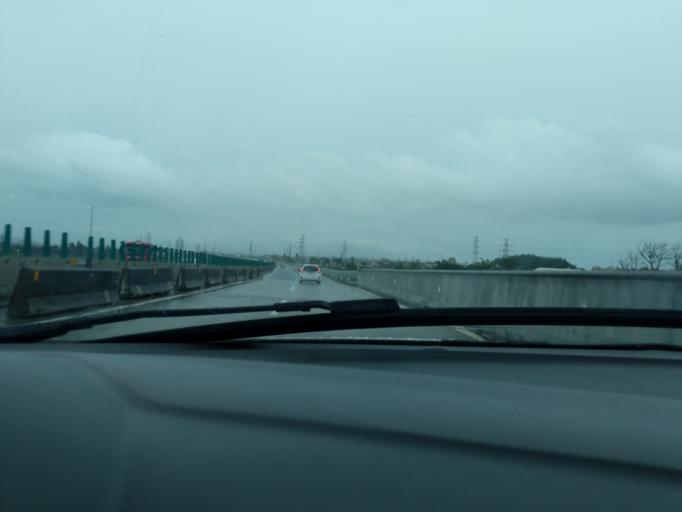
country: CN
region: Guangdong
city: Shuikou
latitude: 22.4643
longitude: 112.7453
